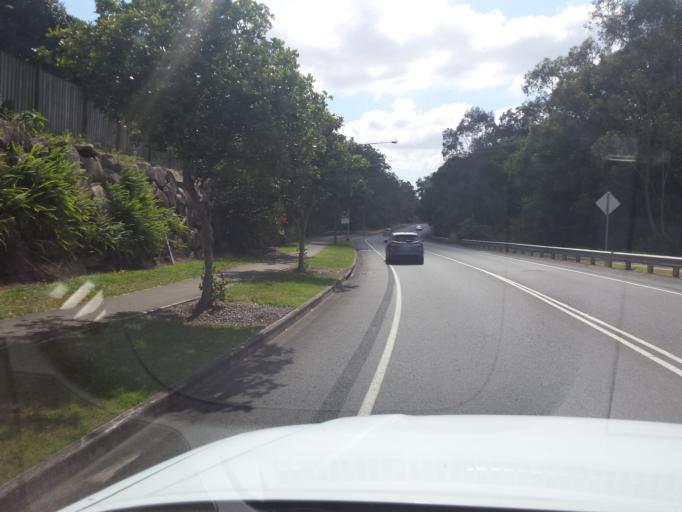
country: AU
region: Queensland
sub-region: Moreton Bay
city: Ferny Hills
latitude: -27.3837
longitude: 152.9638
